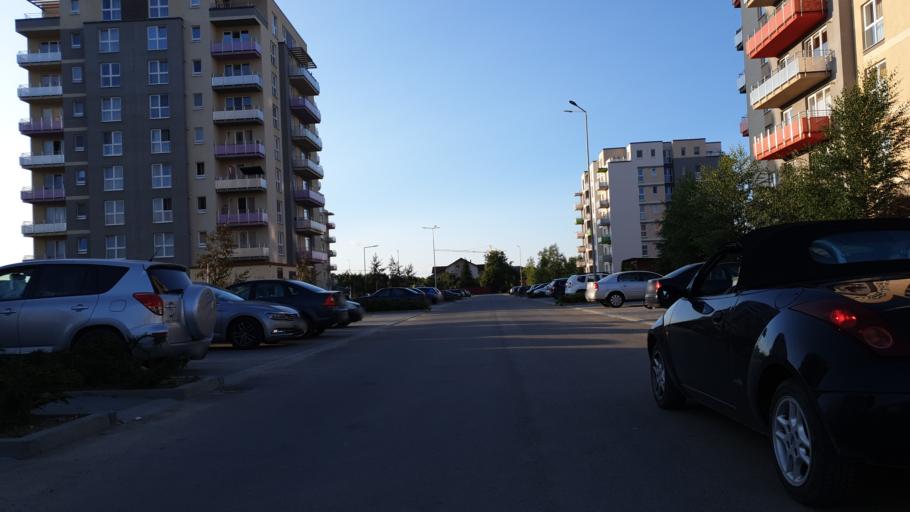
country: RO
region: Brasov
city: Brasov
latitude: 45.6736
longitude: 25.6064
